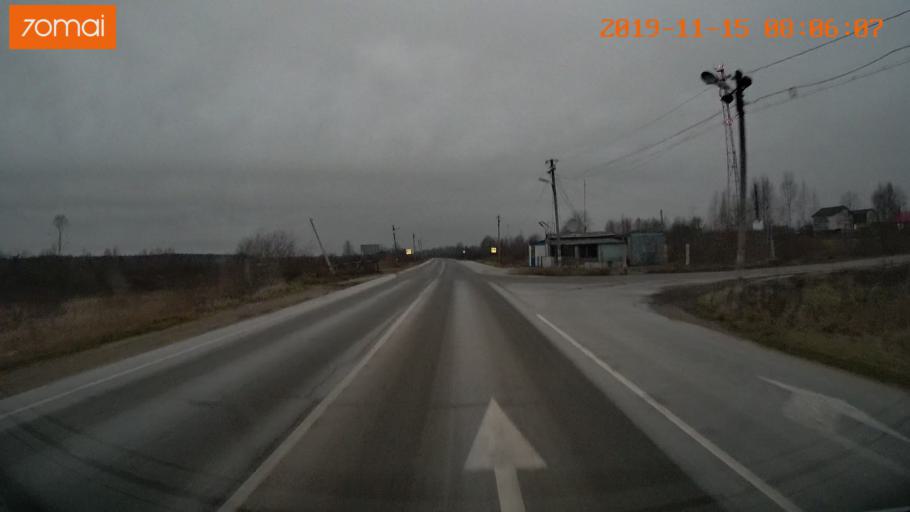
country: RU
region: Vologda
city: Cherepovets
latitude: 59.0207
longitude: 38.0445
